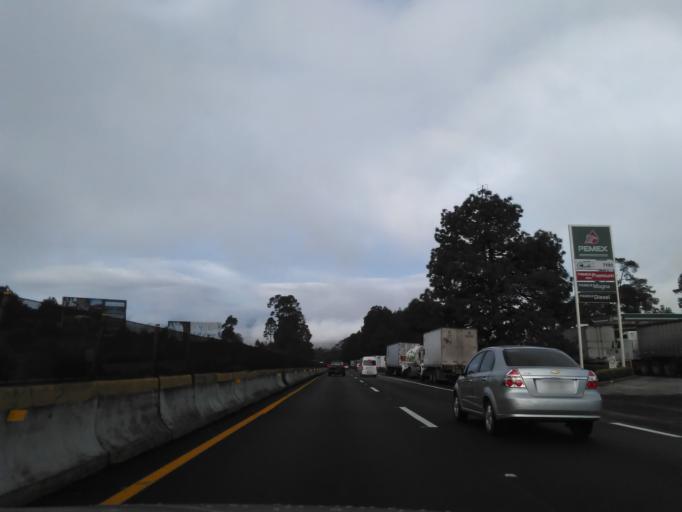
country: MX
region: Morelos
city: Tres Marias
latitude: 19.0844
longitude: -99.2242
